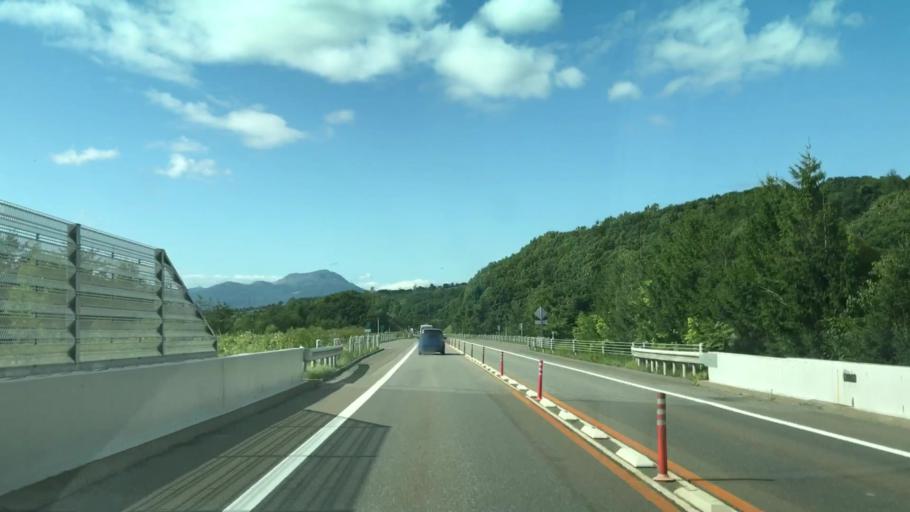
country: JP
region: Hokkaido
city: Date
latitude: 42.4279
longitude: 140.9266
